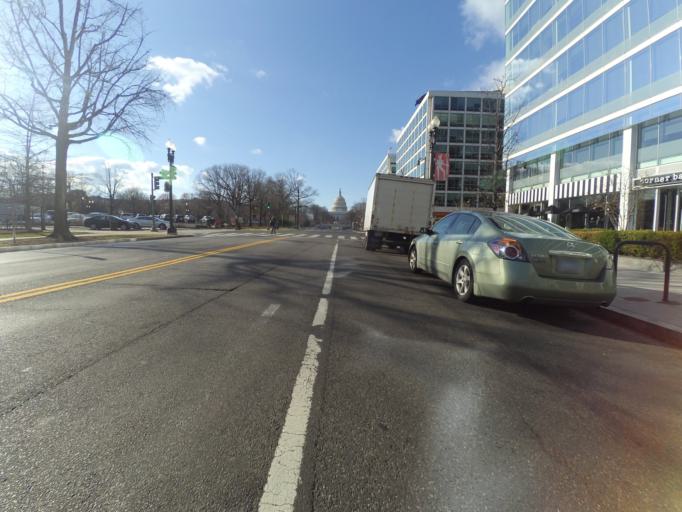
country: US
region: Washington, D.C.
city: Washington, D.C.
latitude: 38.8966
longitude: -77.0092
